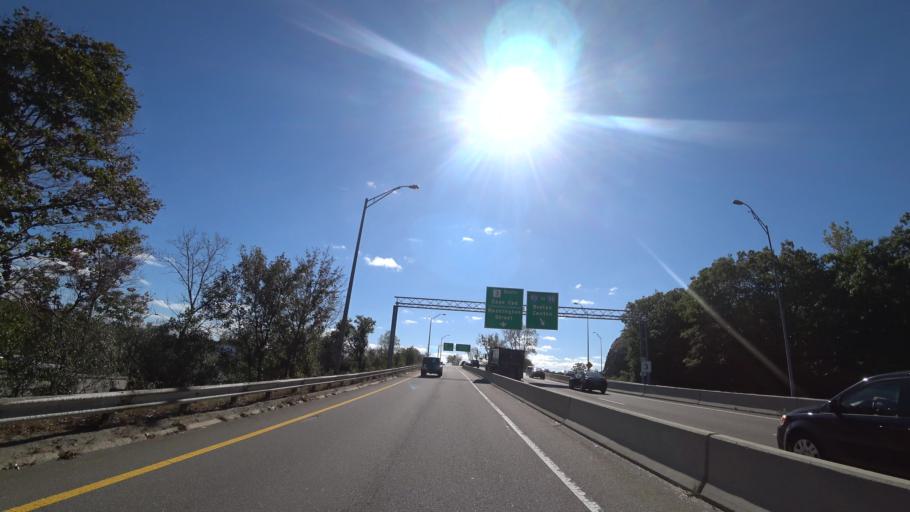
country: US
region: Massachusetts
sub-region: Norfolk County
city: Braintree
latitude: 42.2300
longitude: -71.0111
